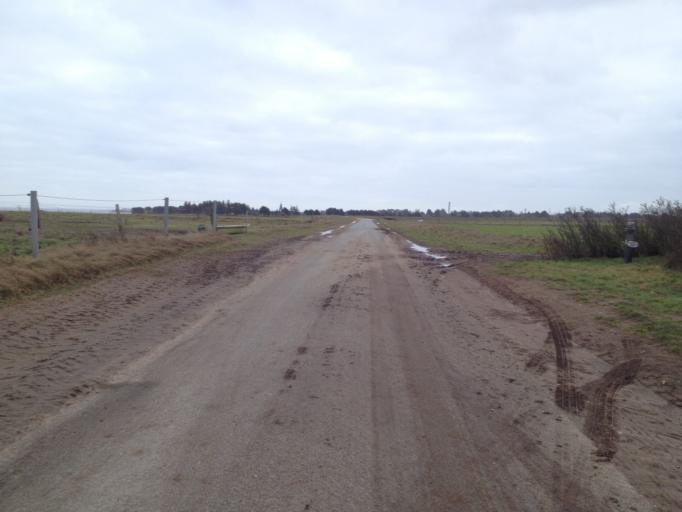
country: DE
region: Schleswig-Holstein
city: Nebel
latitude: 54.6611
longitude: 8.3481
